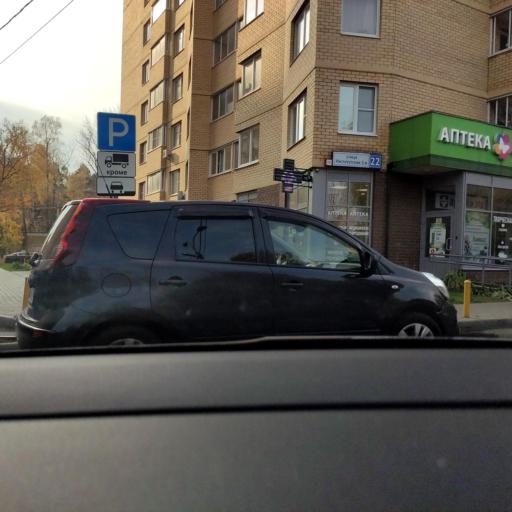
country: RU
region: Moskovskaya
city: Korolev
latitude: 55.9302
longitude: 37.7943
